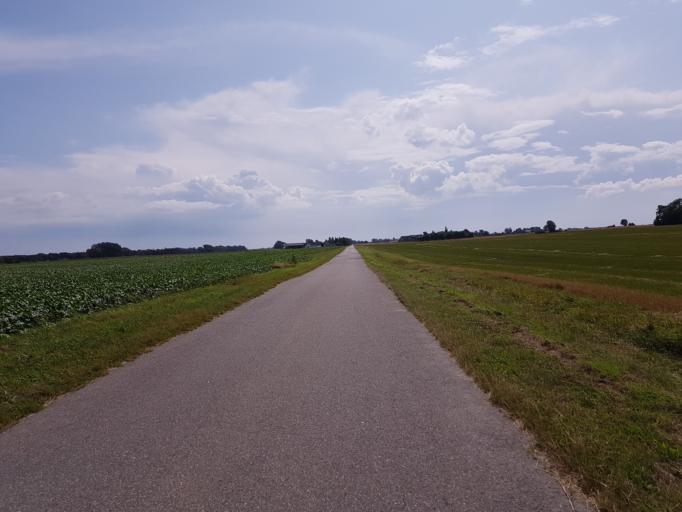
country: DK
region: Zealand
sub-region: Guldborgsund Kommune
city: Nykobing Falster
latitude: 54.5938
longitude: 11.9506
